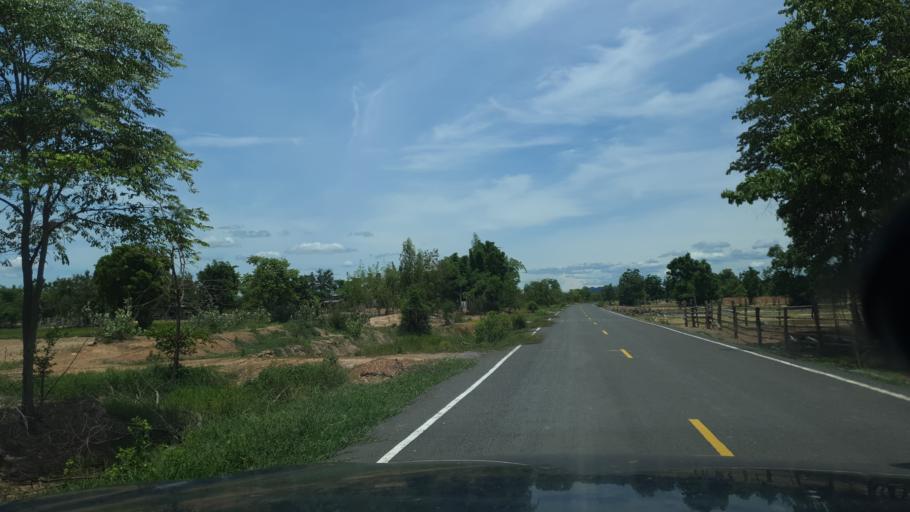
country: TH
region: Sukhothai
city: Ban Na
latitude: 17.1508
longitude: 99.6533
